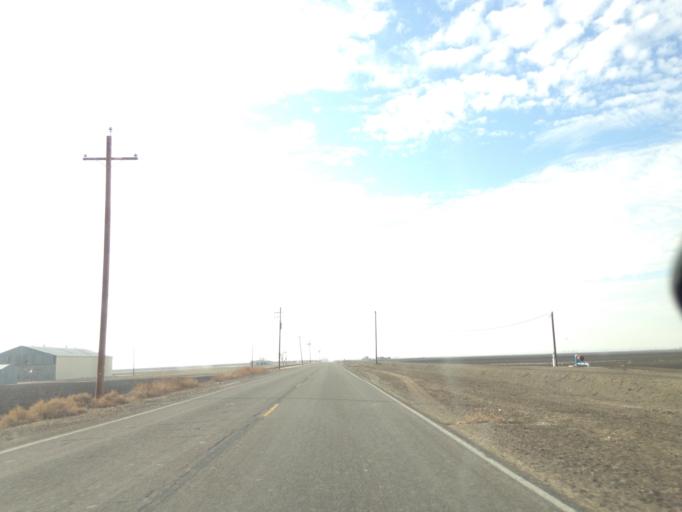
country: US
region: California
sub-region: Kern County
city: Buttonwillow
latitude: 35.4419
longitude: -119.5295
